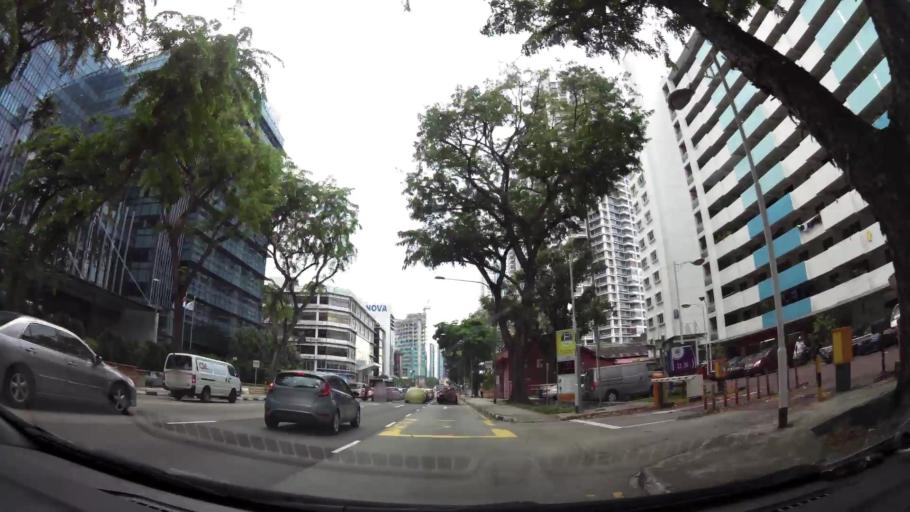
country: SG
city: Singapore
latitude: 1.3176
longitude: 103.8631
